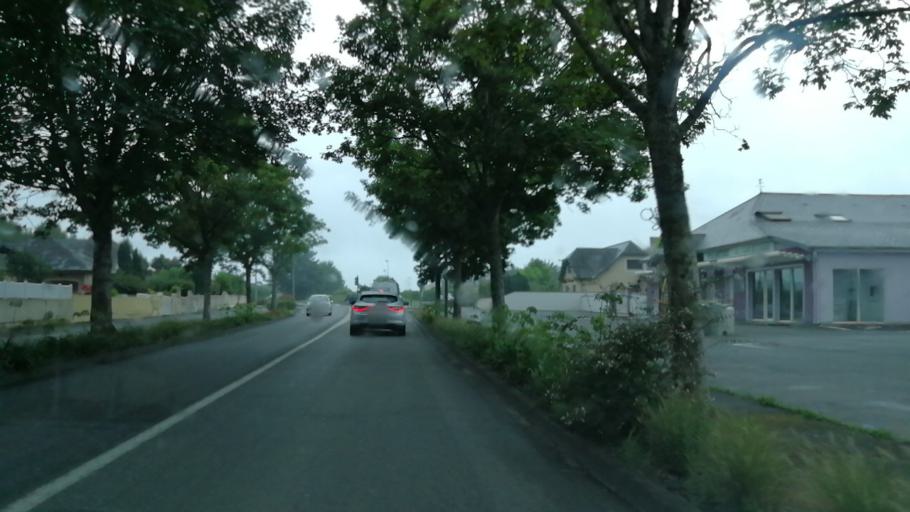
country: FR
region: Aquitaine
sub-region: Departement des Pyrenees-Atlantiques
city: Oloron-Sainte-Marie
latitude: 43.1910
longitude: -0.6203
